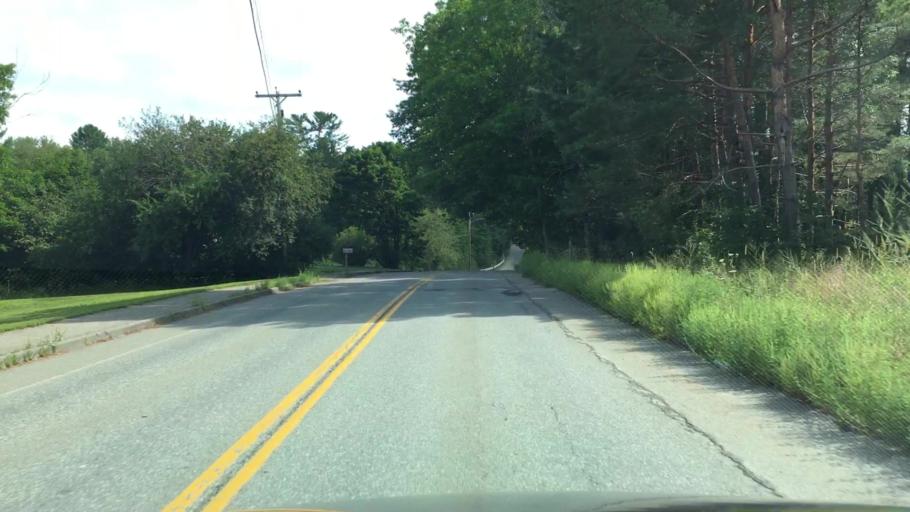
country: US
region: Maine
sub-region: Penobscot County
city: Hampden
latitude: 44.7378
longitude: -68.8607
